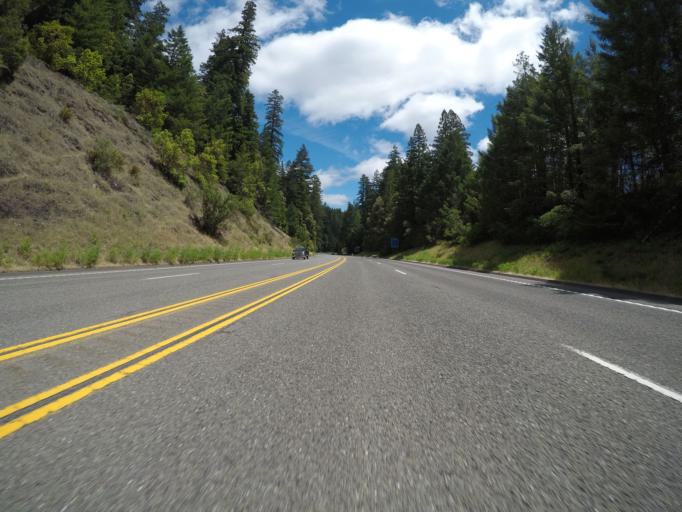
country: US
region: California
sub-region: Humboldt County
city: Redway
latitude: 40.2735
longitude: -123.8797
